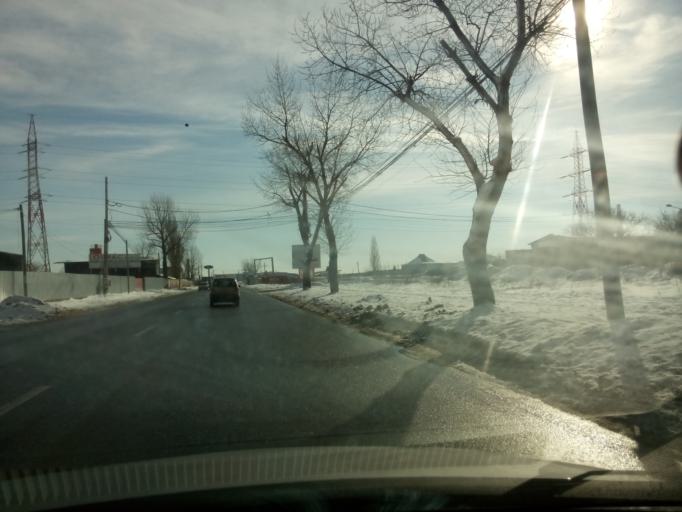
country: RO
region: Ilfov
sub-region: Comuna Popesti-Leordeni
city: Popesti-Leordeni
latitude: 44.3705
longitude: 26.1824
